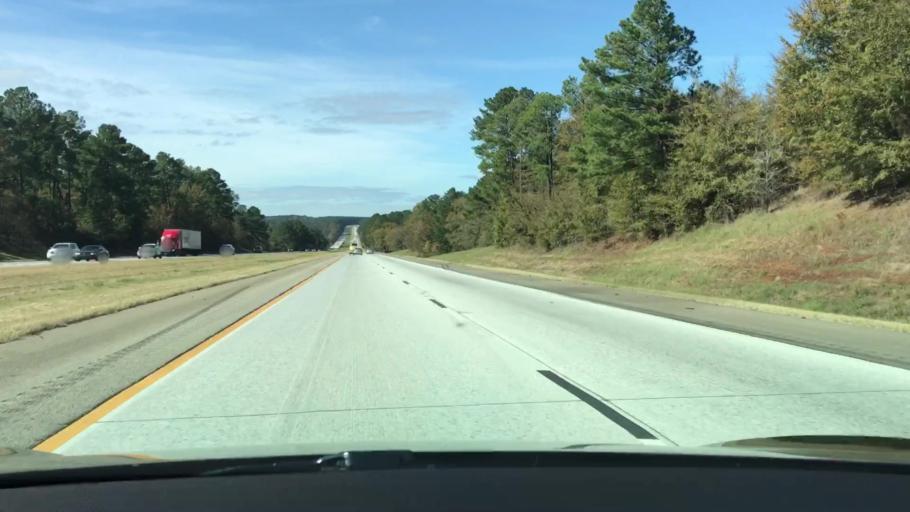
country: US
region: Georgia
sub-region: Greene County
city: Greensboro
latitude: 33.5352
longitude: -83.2573
